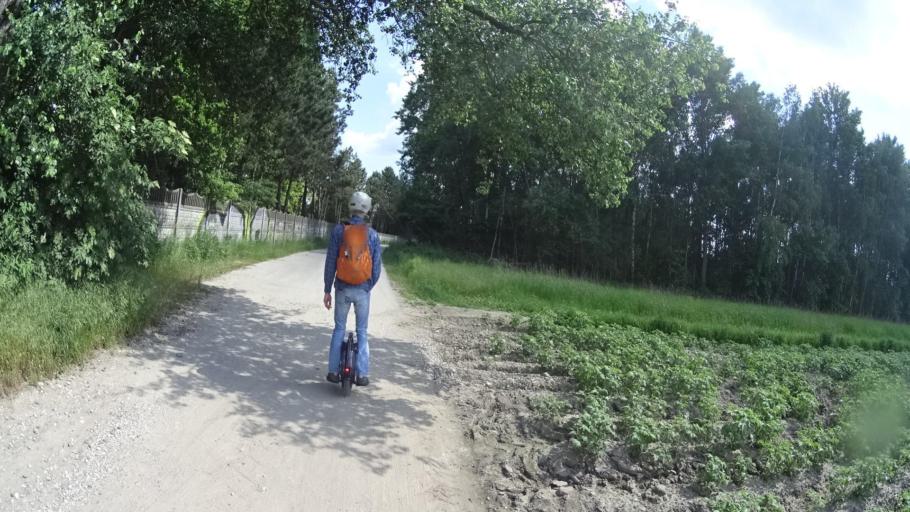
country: PL
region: Masovian Voivodeship
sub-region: Warszawa
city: Kabaty
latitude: 52.1097
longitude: 21.0890
